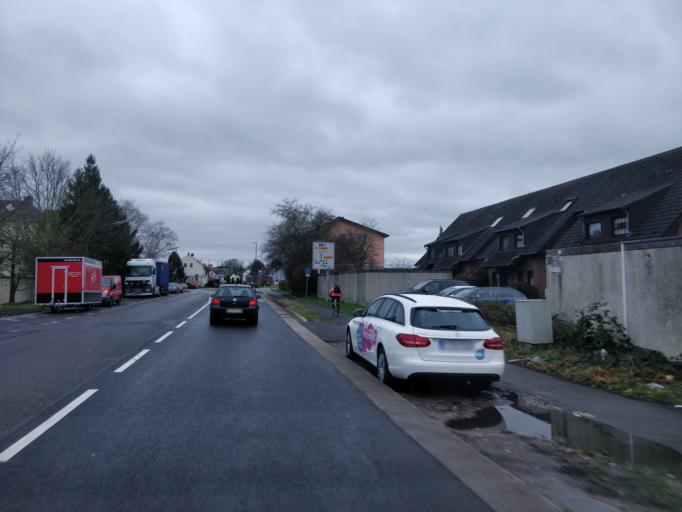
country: DE
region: North Rhine-Westphalia
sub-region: Regierungsbezirk Koln
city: Wahn-Heide
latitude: 50.8642
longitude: 7.0838
